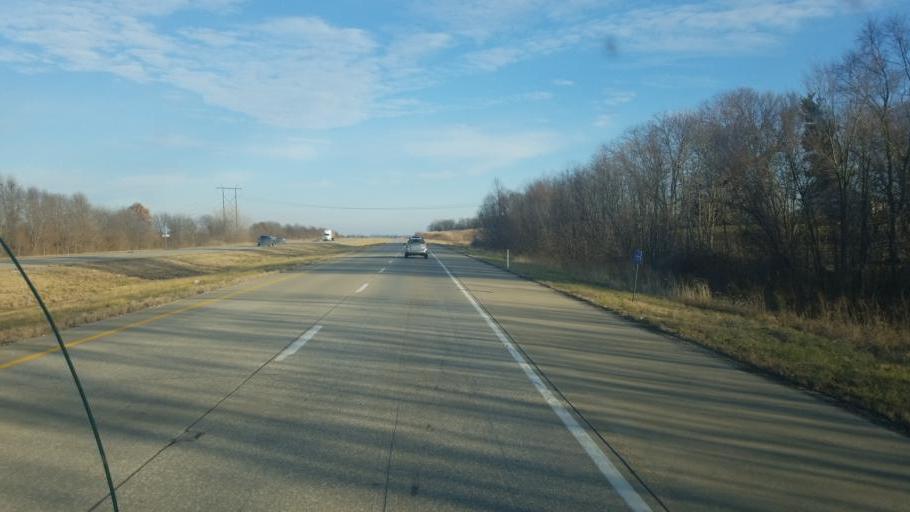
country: US
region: Indiana
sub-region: Knox County
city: Vincennes
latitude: 38.6787
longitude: -87.4001
